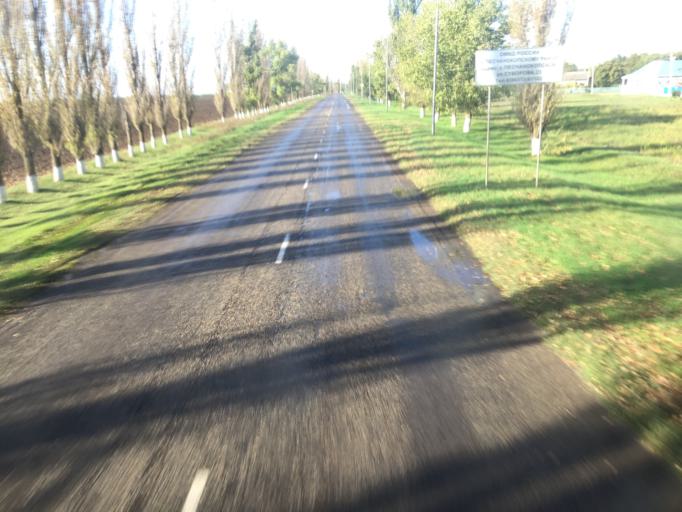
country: RU
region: Rostov
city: Peschanokopskoye
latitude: 46.1971
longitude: 41.1163
